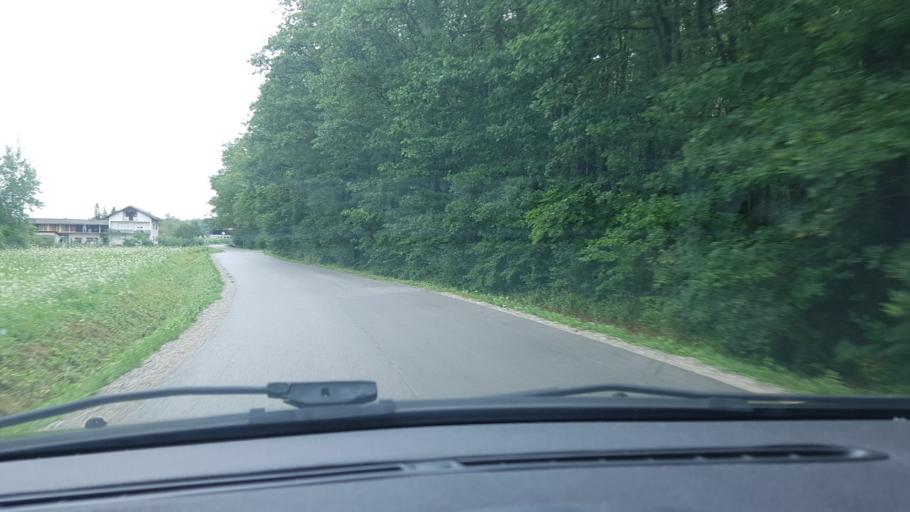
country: HR
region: Karlovacka
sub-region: Grad Karlovac
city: Karlovac
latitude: 45.5648
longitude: 15.5449
